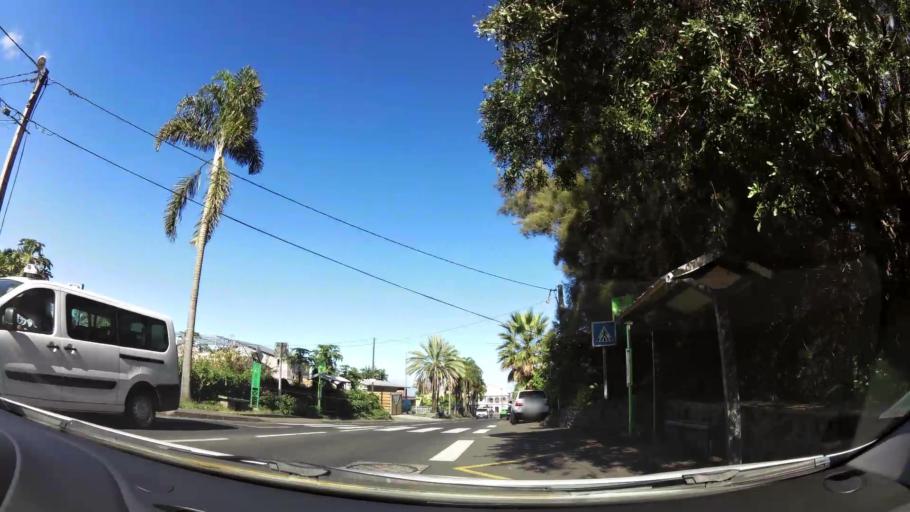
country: RE
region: Reunion
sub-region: Reunion
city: Le Tampon
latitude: -21.2665
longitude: 55.5250
